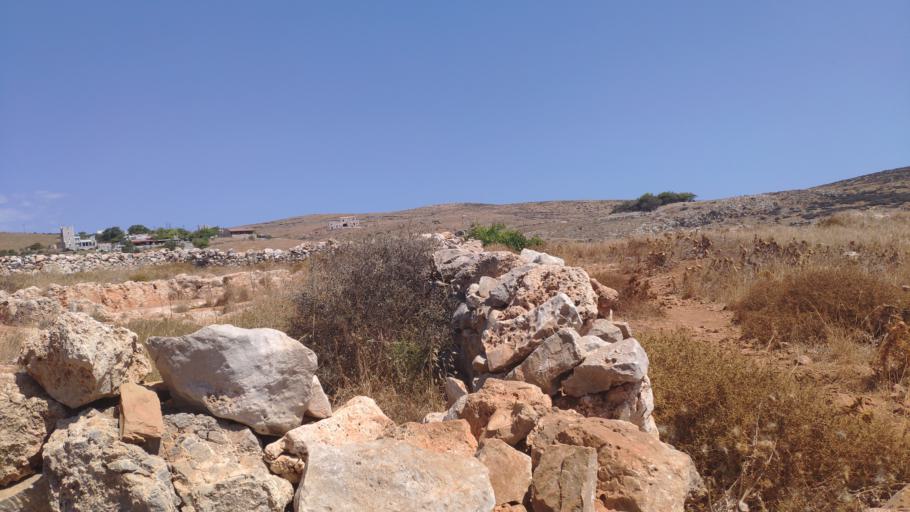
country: GR
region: Peloponnese
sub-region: Nomos Lakonias
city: Gytheio
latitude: 36.4003
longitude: 22.4851
